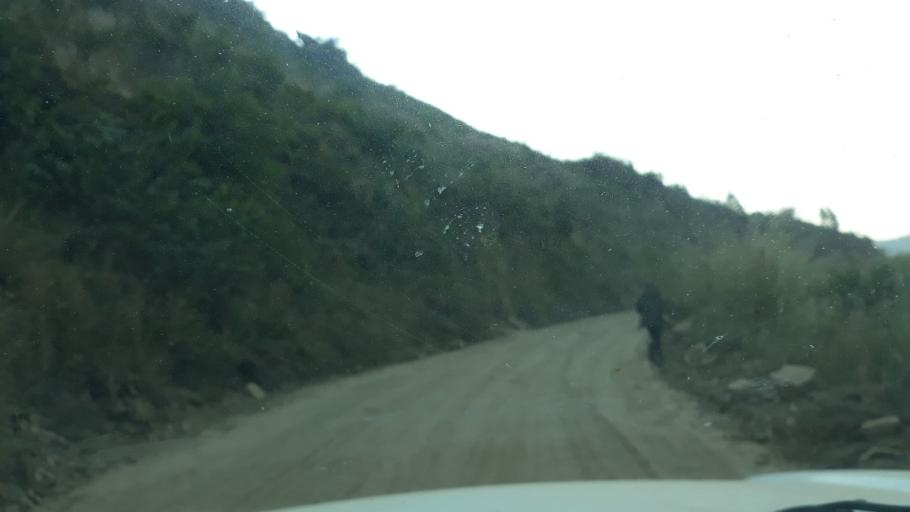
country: RW
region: Western Province
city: Cyangugu
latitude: -2.7016
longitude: 28.9534
